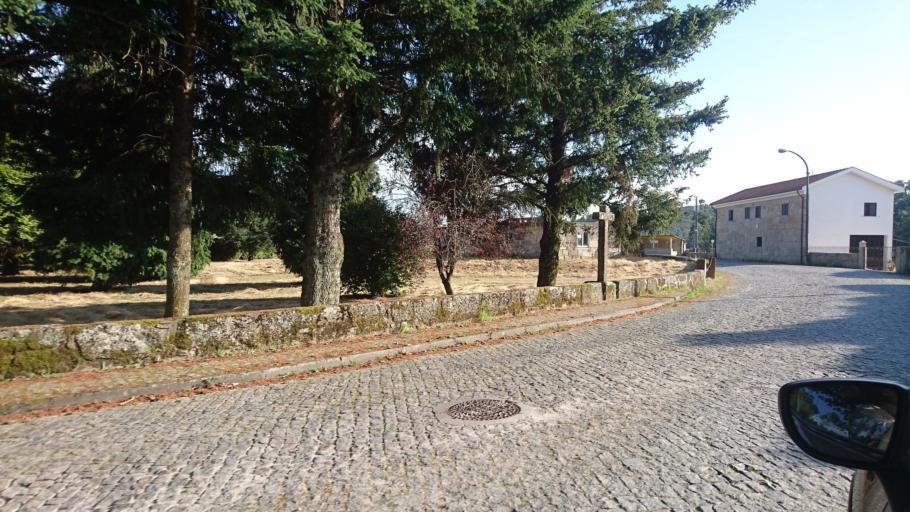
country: PT
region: Porto
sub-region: Paredes
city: Recarei
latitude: 41.1280
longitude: -8.3684
